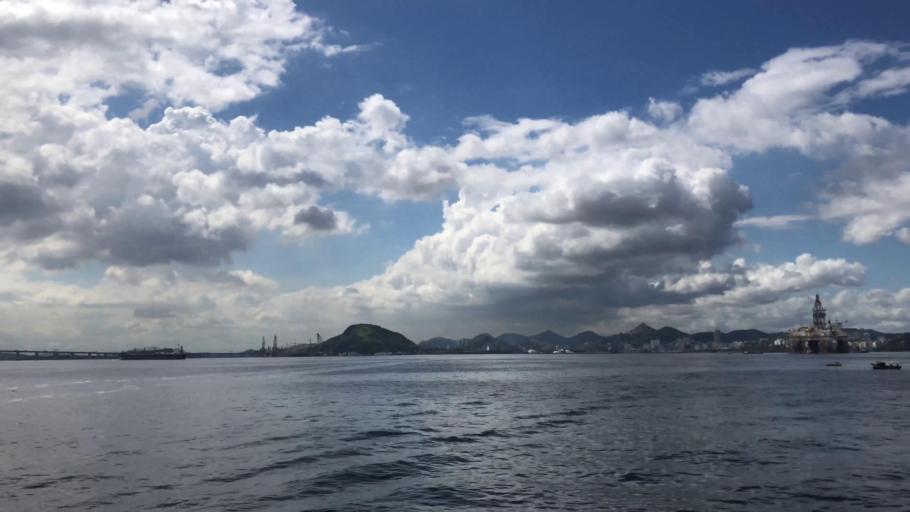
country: BR
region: Rio de Janeiro
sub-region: Rio De Janeiro
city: Rio de Janeiro
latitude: -22.8987
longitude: -43.1562
